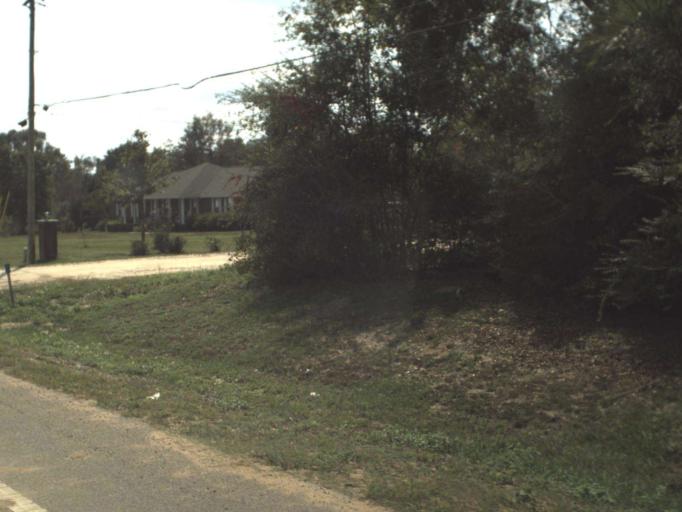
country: US
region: Florida
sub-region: Holmes County
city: Bonifay
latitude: 30.7548
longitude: -85.6849
